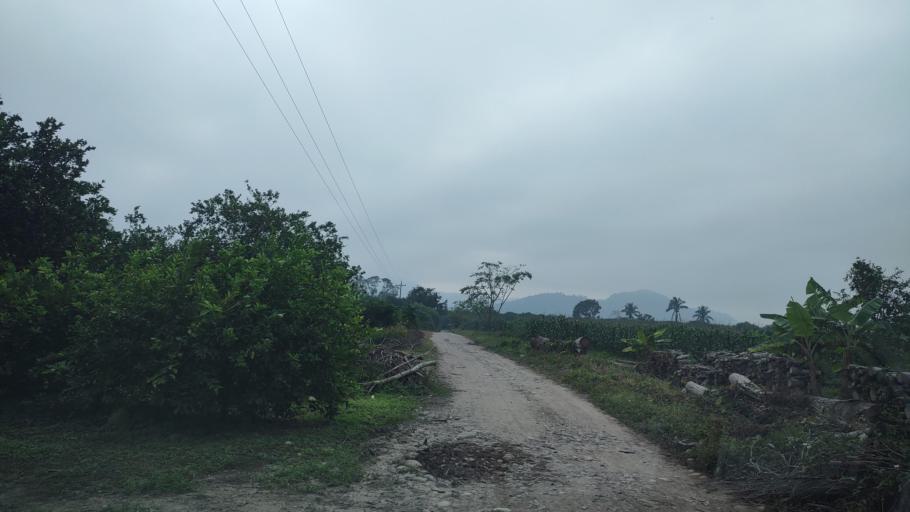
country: MX
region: Veracruz
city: Agua Dulce
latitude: 20.3301
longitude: -97.2850
